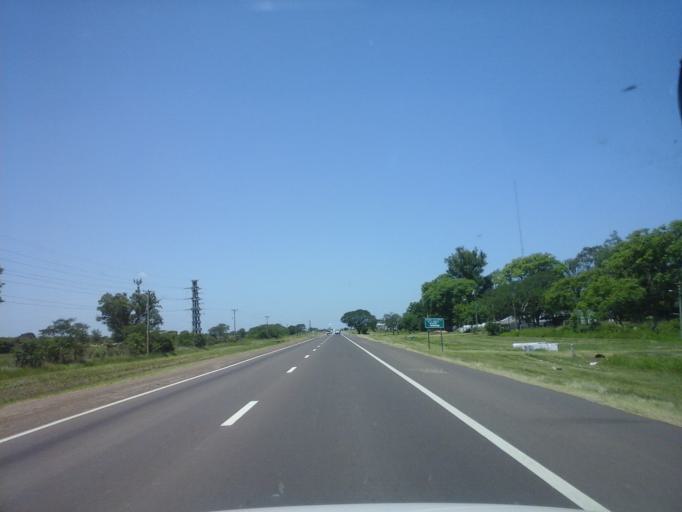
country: AR
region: Corrientes
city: Corrientes
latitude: -27.4262
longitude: -58.7150
